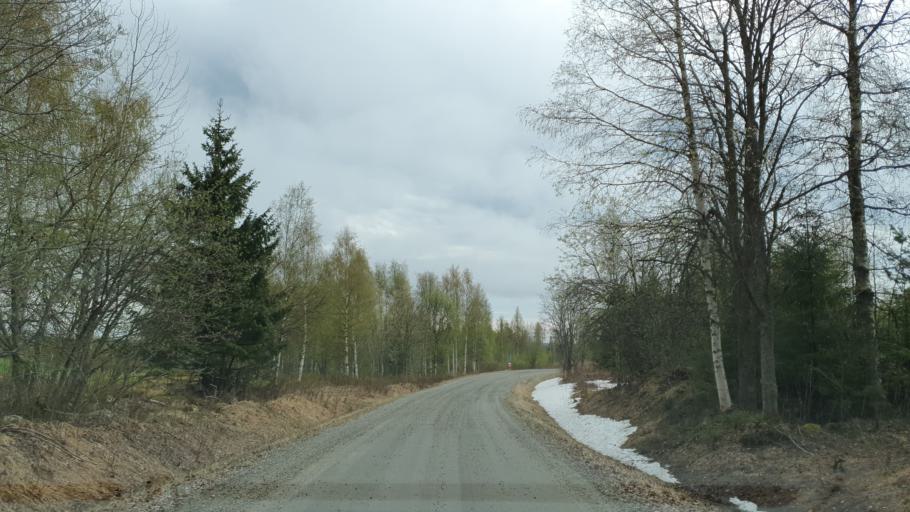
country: FI
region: Kainuu
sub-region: Kehys-Kainuu
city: Kuhmo
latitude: 64.1393
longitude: 29.9680
